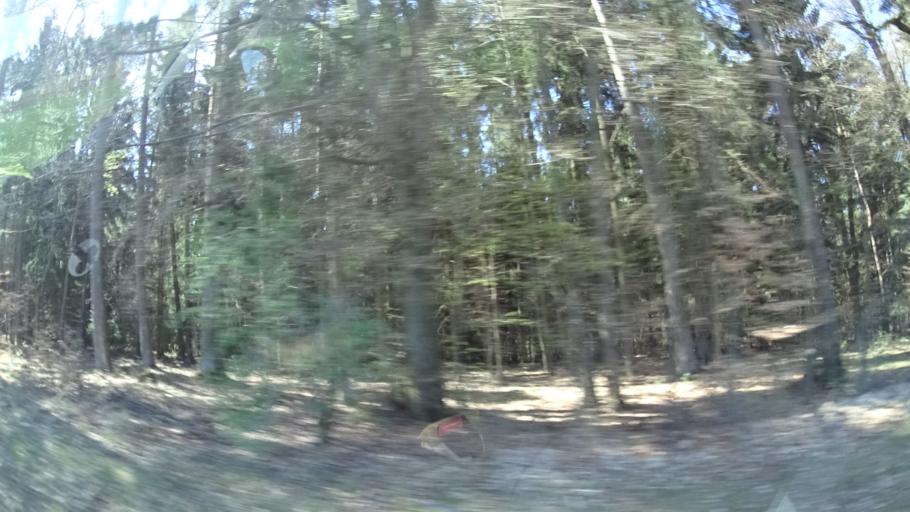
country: DE
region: Bavaria
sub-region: Regierungsbezirk Mittelfranken
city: Alfeld
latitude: 49.4185
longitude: 11.5627
